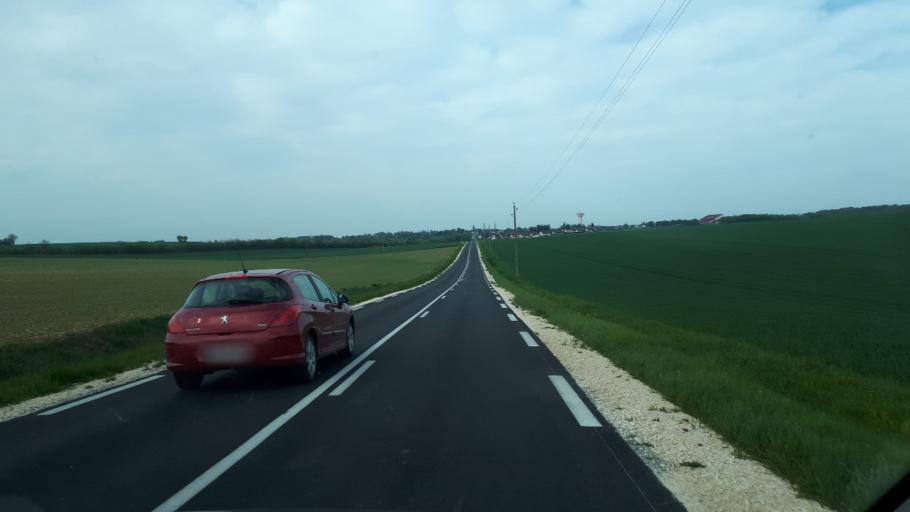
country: FR
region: Centre
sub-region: Departement du Cher
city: Rians
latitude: 47.2082
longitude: 2.5981
